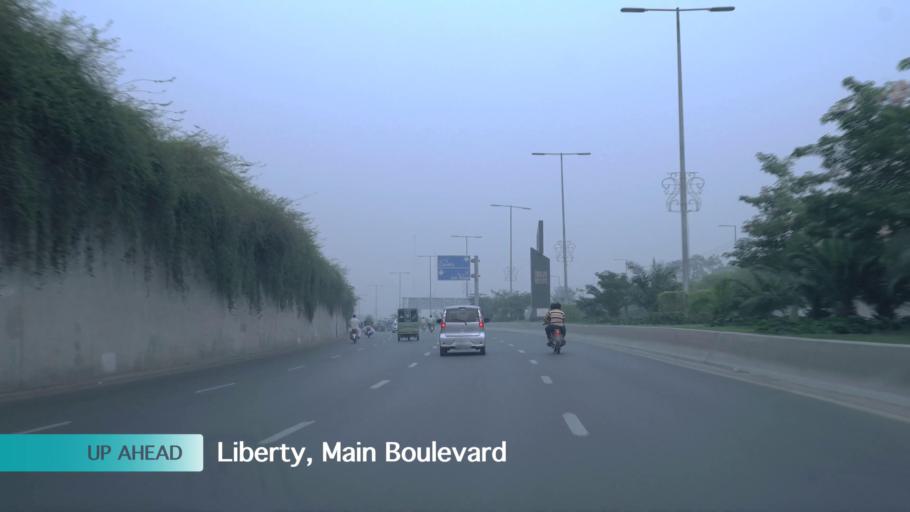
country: PK
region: Punjab
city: Lahore
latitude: 31.5048
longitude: 74.3331
